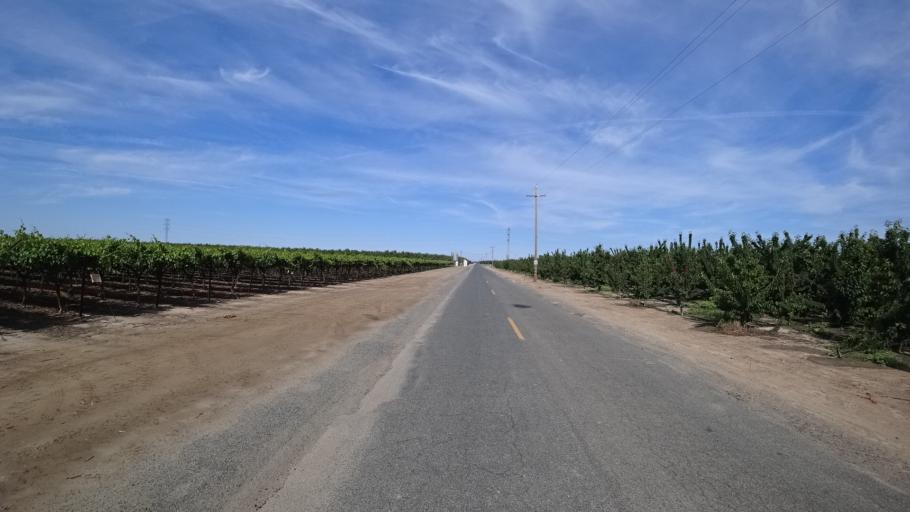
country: US
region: California
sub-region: Kings County
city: Lucerne
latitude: 36.4158
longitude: -119.5896
